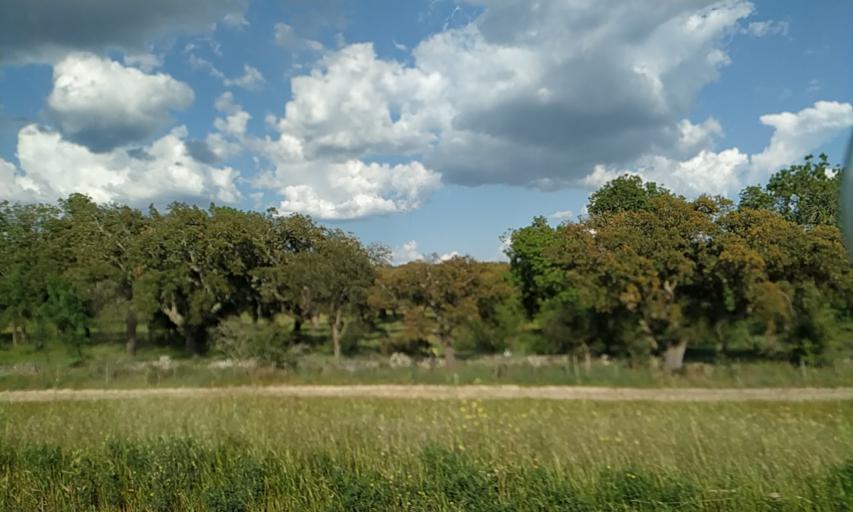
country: PT
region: Portalegre
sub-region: Portalegre
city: Urra
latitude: 39.2205
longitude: -7.4575
